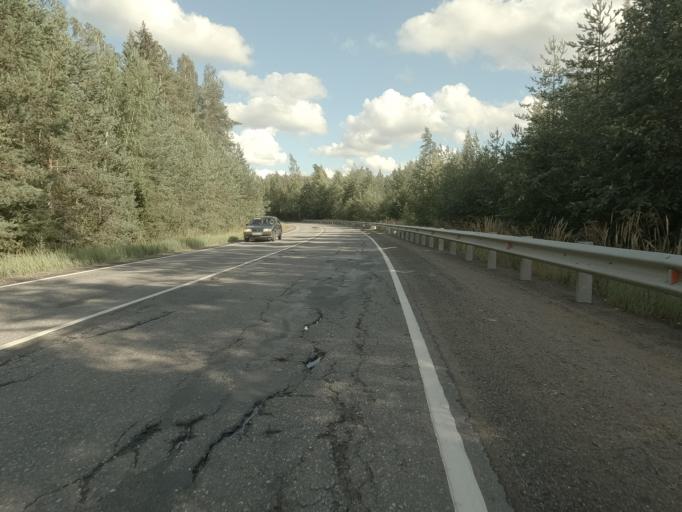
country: RU
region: Leningrad
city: Borisova Griva
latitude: 59.9859
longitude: 30.8899
